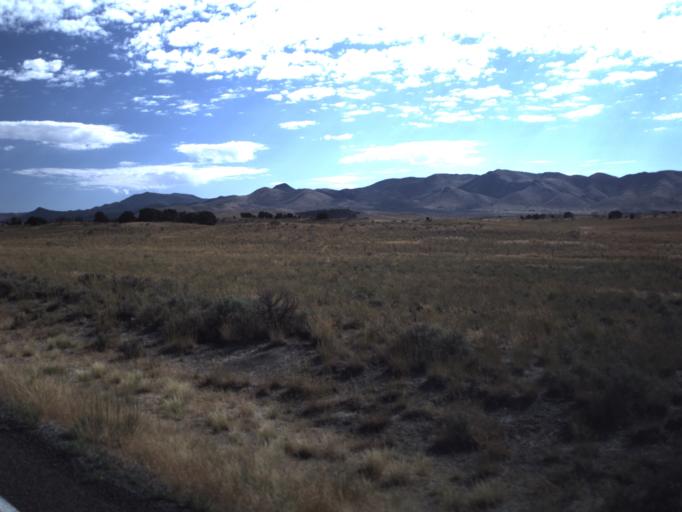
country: US
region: Utah
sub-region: Juab County
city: Mona
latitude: 39.7294
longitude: -112.1944
